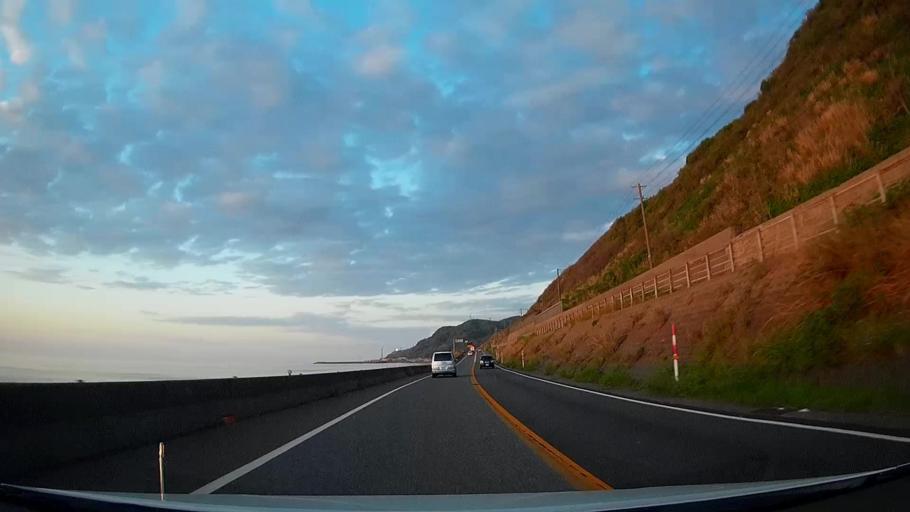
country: JP
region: Niigata
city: Joetsu
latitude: 37.1488
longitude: 138.0690
